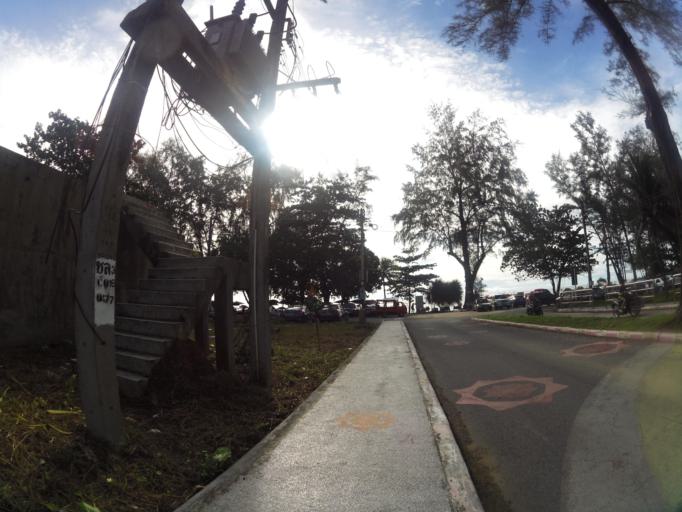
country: TH
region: Phuket
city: Thalang
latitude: 7.9754
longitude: 98.2793
